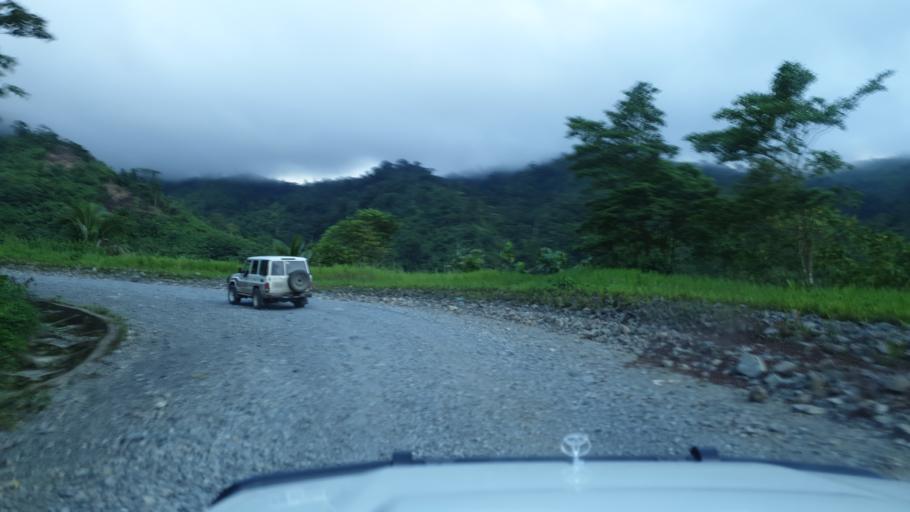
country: PG
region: Bougainville
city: Panguna
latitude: -6.3362
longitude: 155.4636
